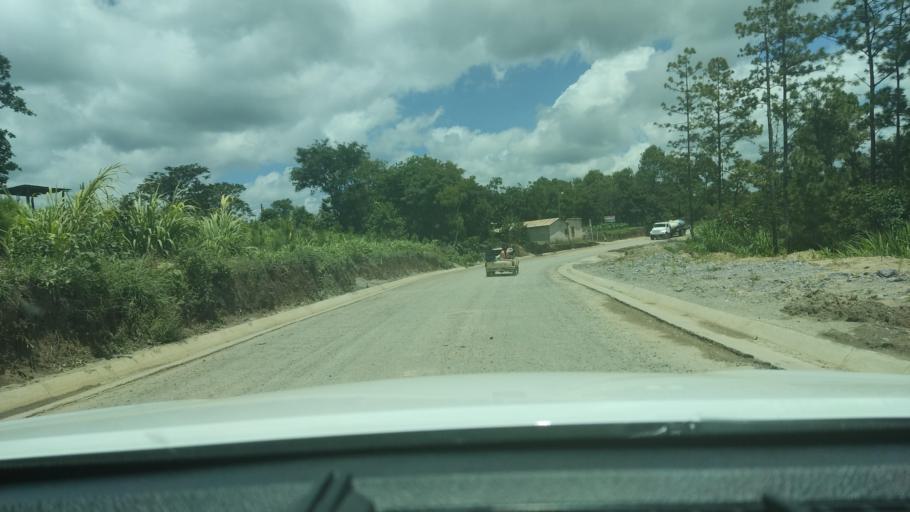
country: GT
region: Chimaltenango
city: San Martin Jilotepeque
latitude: 14.7914
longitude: -90.8071
